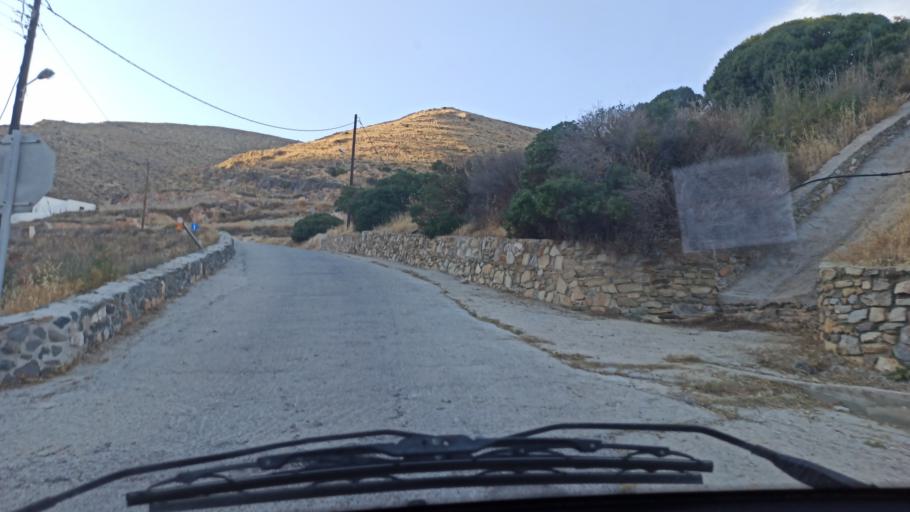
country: GR
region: South Aegean
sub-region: Nomos Kykladon
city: Ano Syros
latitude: 37.4529
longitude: 24.9366
